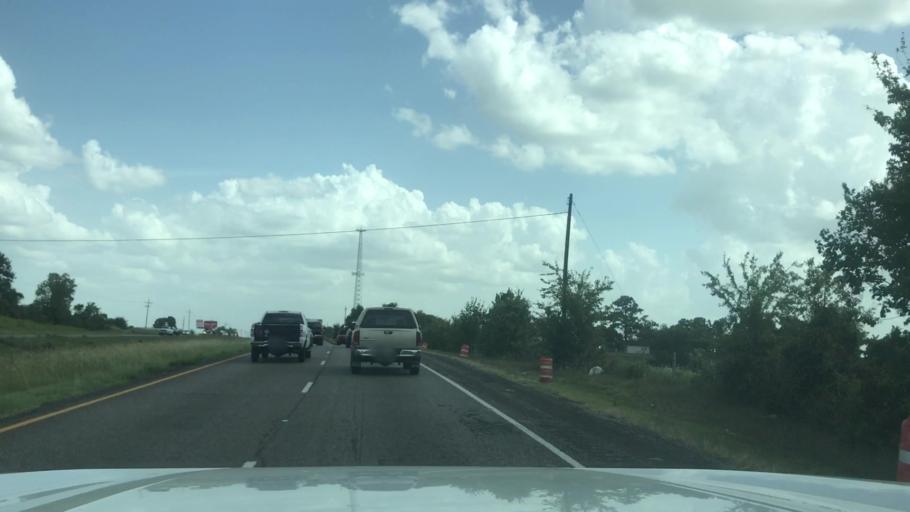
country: US
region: Texas
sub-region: Grimes County
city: Navasota
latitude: 30.2813
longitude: -96.0450
